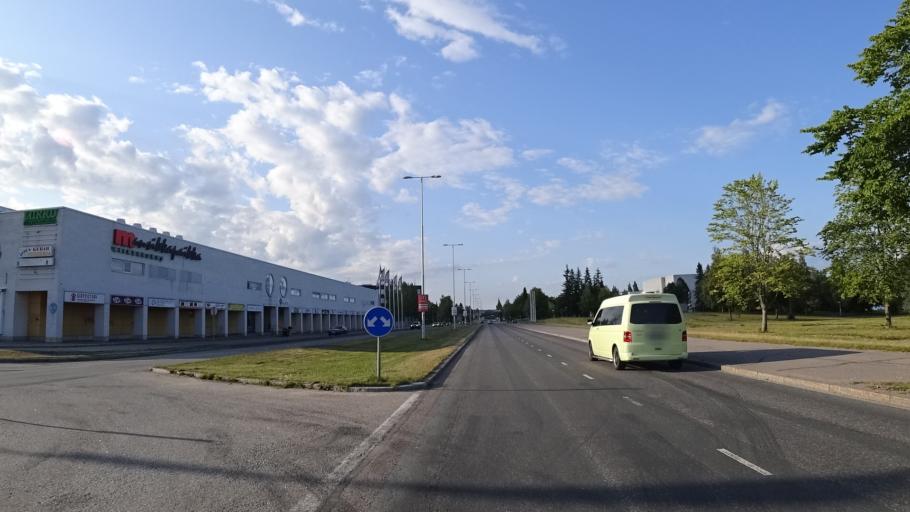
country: FI
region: South Karelia
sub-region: Imatra
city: Imatra
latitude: 61.1896
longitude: 28.7773
